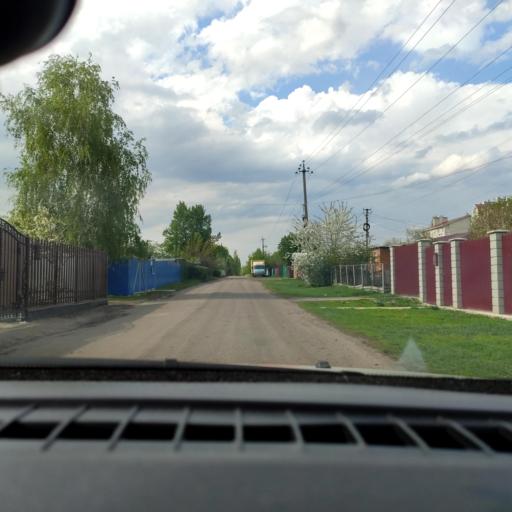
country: RU
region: Voronezj
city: Maslovka
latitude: 51.5343
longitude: 39.3378
